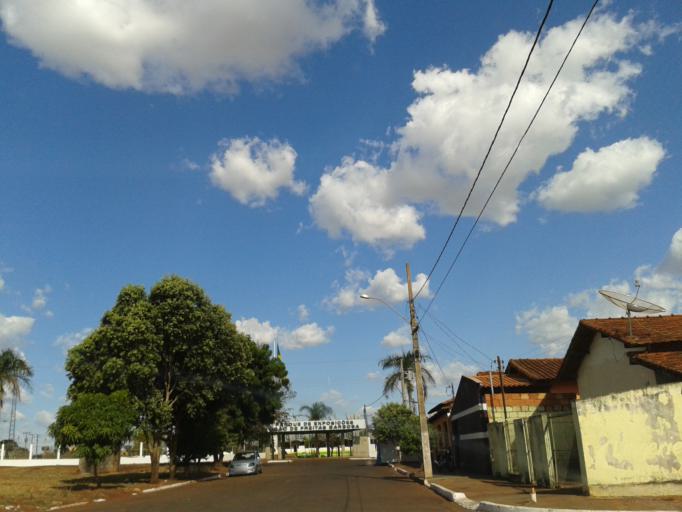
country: BR
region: Minas Gerais
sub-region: Capinopolis
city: Capinopolis
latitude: -18.6929
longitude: -49.5673
